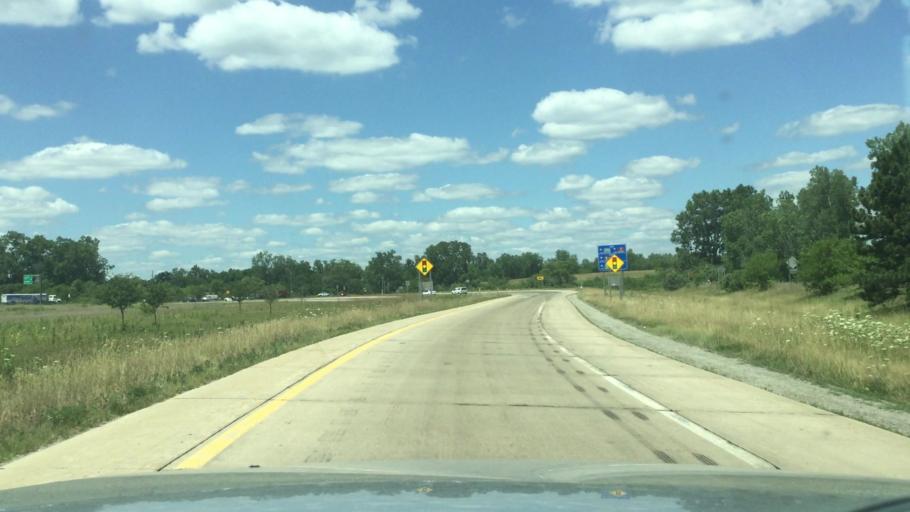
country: US
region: Michigan
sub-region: Wayne County
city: Belleville
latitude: 42.2194
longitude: -83.5431
